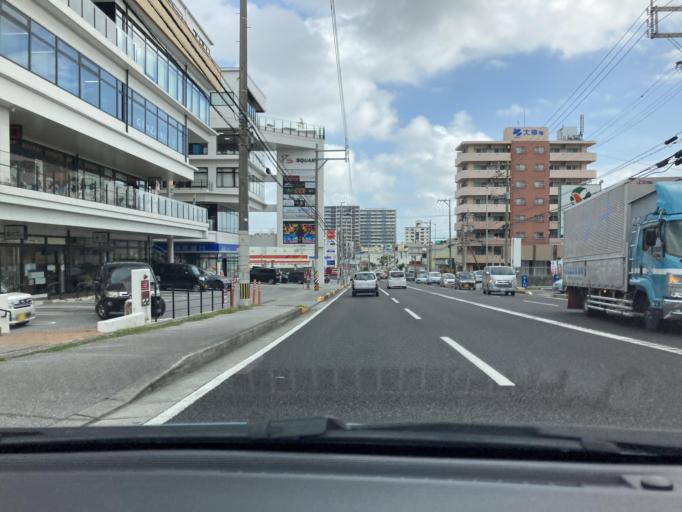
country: JP
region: Okinawa
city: Ginowan
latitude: 26.2557
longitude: 127.7401
